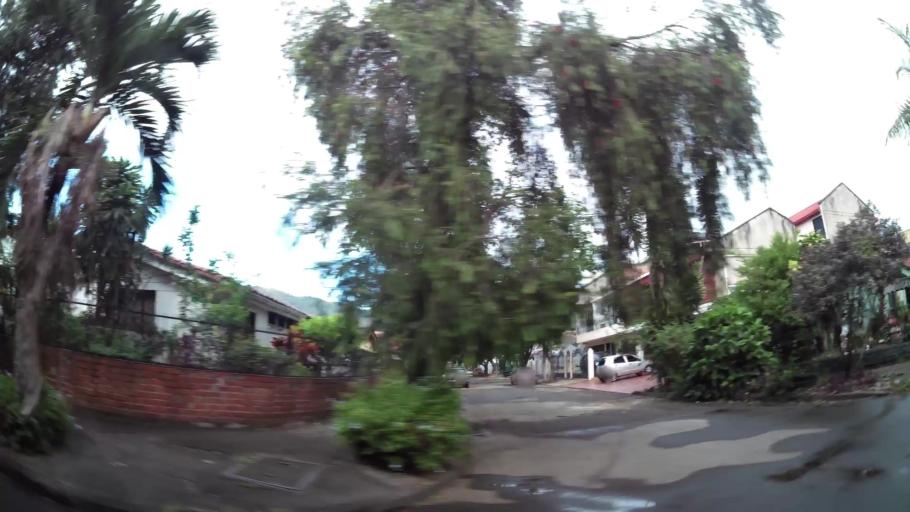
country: CO
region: Valle del Cauca
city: Cali
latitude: 3.4772
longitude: -76.5199
